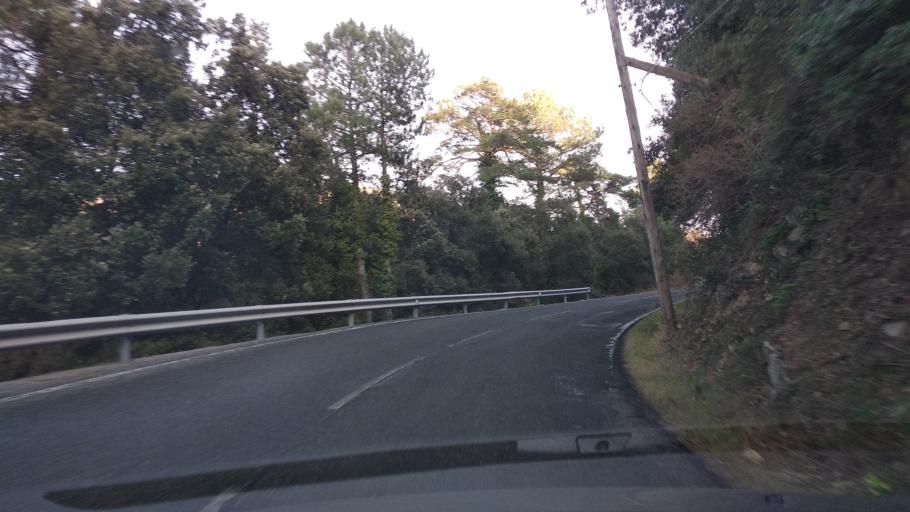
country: ES
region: Catalonia
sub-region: Provincia de Tarragona
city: Alforja
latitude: 41.2230
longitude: 0.9264
